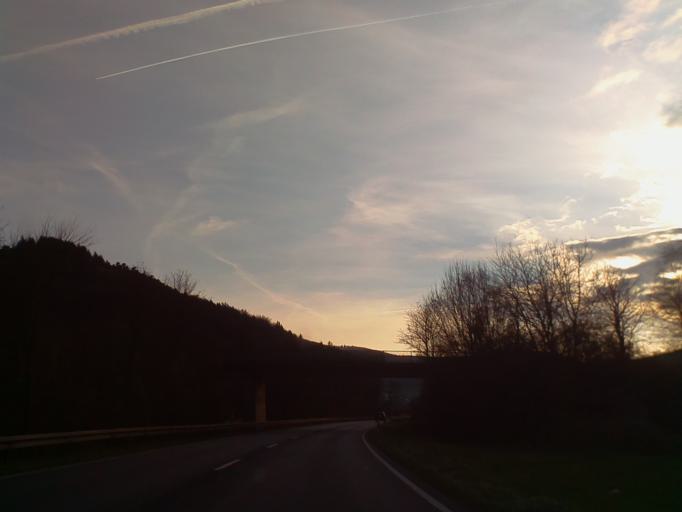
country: DE
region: Bavaria
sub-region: Regierungsbezirk Unterfranken
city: Weilbach
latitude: 49.6618
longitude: 9.2120
